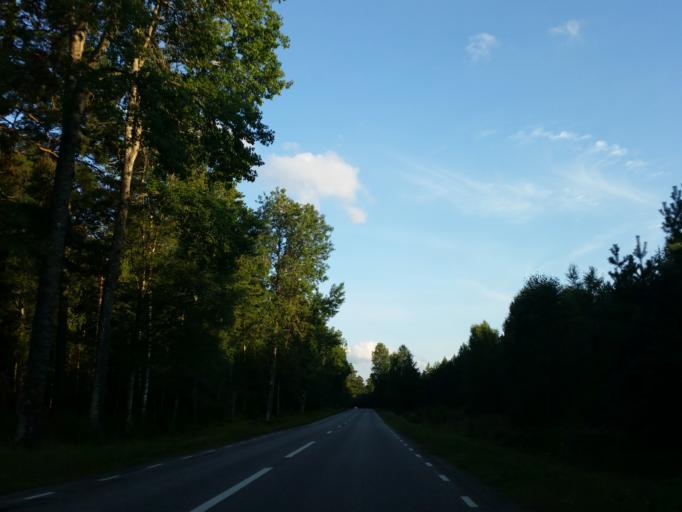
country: SE
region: Stockholm
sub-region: Sodertalje Kommun
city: Soedertaelje
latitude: 59.2436
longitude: 17.5412
